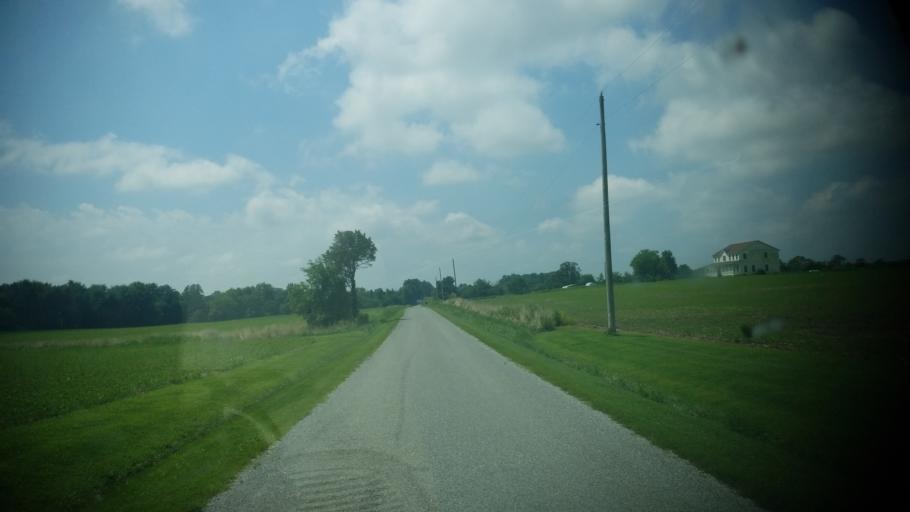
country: US
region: Illinois
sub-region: Wayne County
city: Fairfield
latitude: 38.5291
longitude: -88.3654
